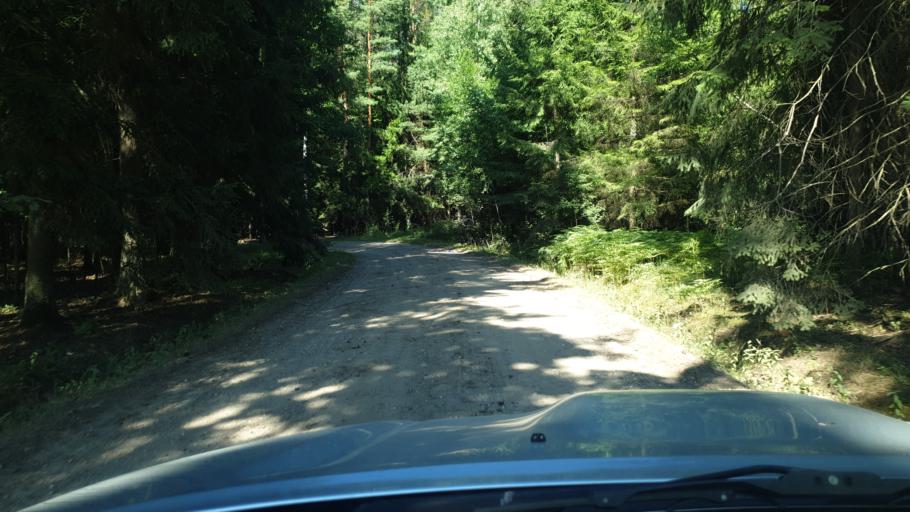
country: LT
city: Sirvintos
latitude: 54.9132
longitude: 24.9271
